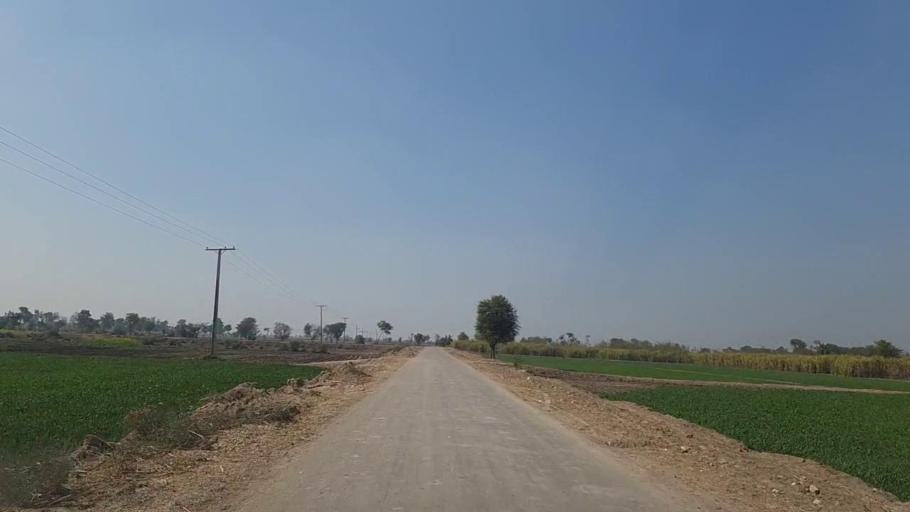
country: PK
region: Sindh
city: Daur
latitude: 26.5033
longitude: 68.3162
